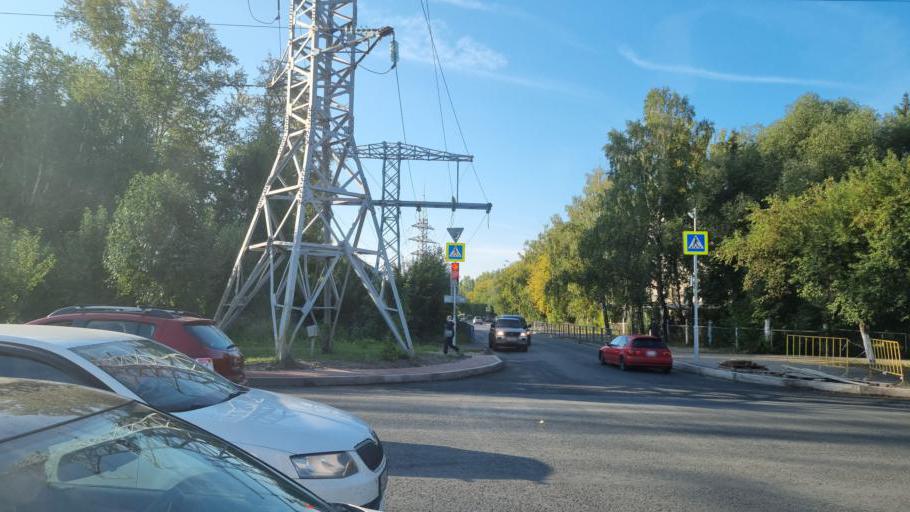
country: RU
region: Tomsk
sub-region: Tomskiy Rayon
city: Tomsk
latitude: 56.4552
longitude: 84.9628
